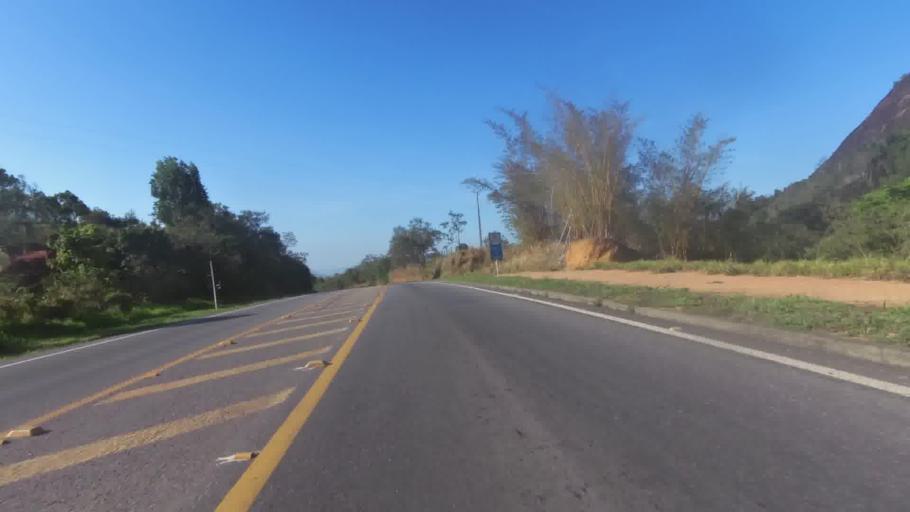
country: BR
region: Espirito Santo
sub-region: Alfredo Chaves
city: Alfredo Chaves
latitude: -20.7046
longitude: -40.7175
